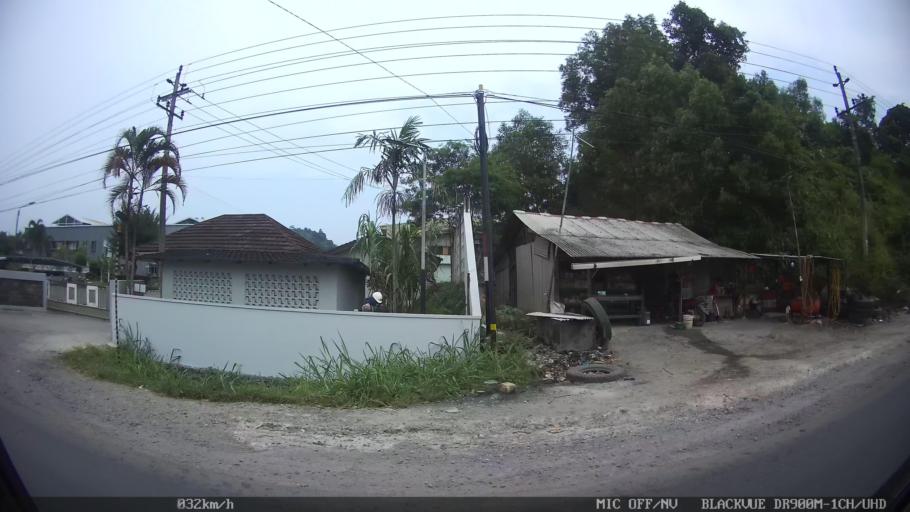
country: ID
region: Lampung
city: Panjang
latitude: -5.4153
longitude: 105.3451
